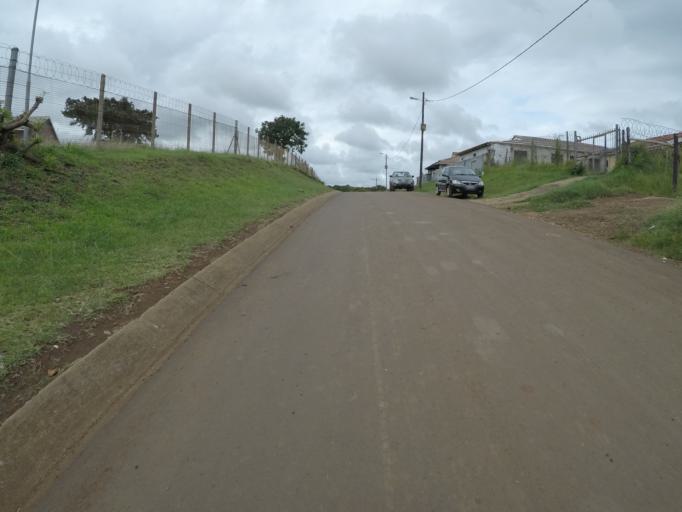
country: ZA
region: KwaZulu-Natal
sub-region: uThungulu District Municipality
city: Empangeni
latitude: -28.7795
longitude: 31.8676
